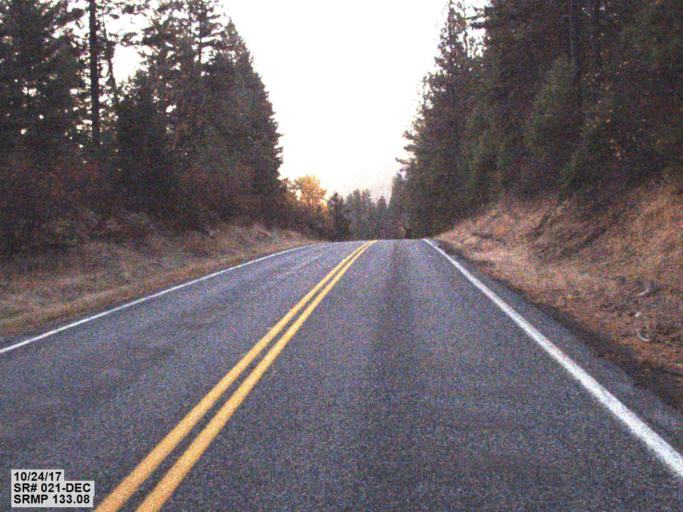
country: US
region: Washington
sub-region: Ferry County
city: Republic
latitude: 48.2936
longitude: -118.7326
